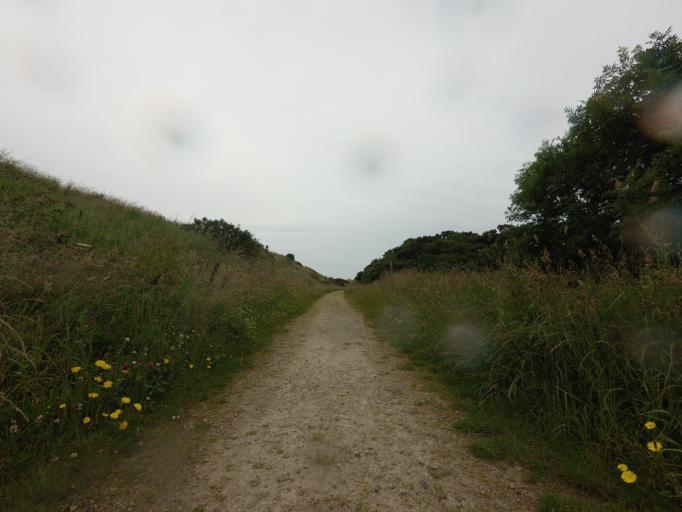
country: GB
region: Scotland
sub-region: Moray
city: Portknockie
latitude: 57.6968
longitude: -2.8496
